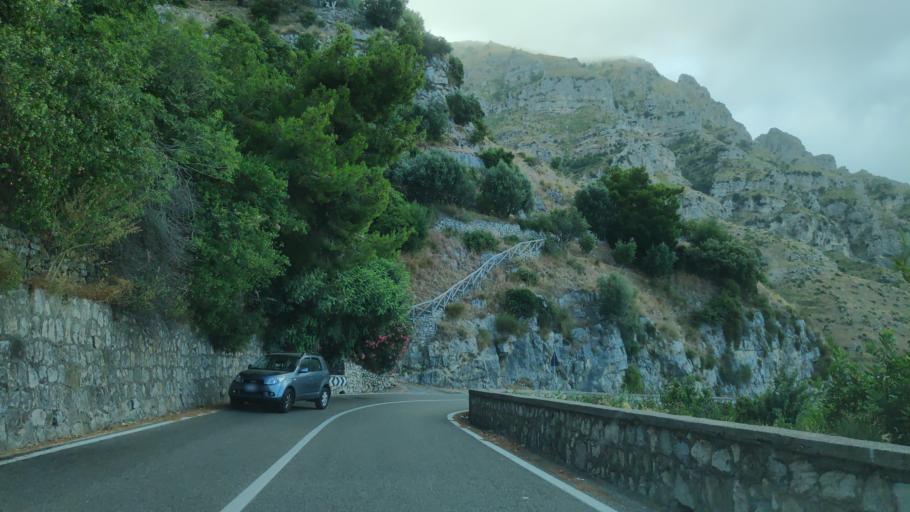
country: IT
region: Campania
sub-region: Provincia di Napoli
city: Arola-Preazzano
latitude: 40.6199
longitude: 14.4500
